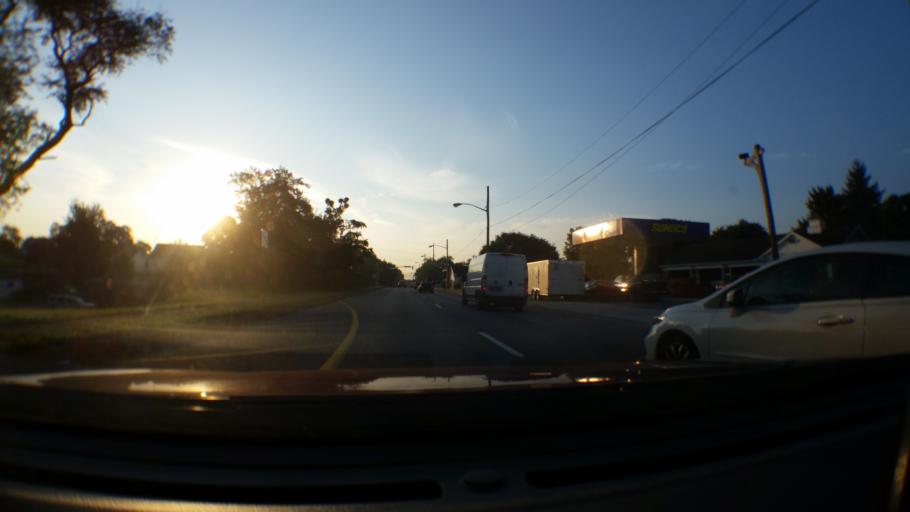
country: US
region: Maryland
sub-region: Washington County
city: Hagerstown
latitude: 39.6513
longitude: -77.7382
